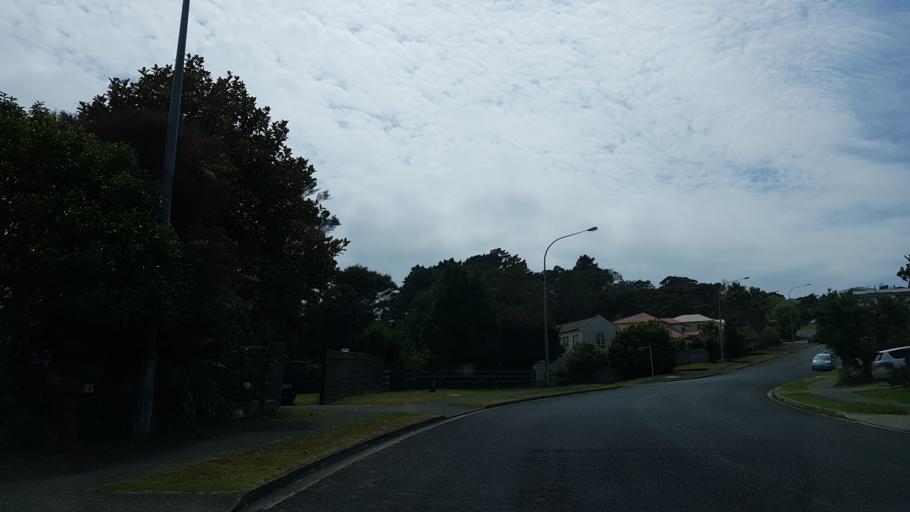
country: NZ
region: Auckland
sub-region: Auckland
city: North Shore
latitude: -36.7693
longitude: 174.7087
